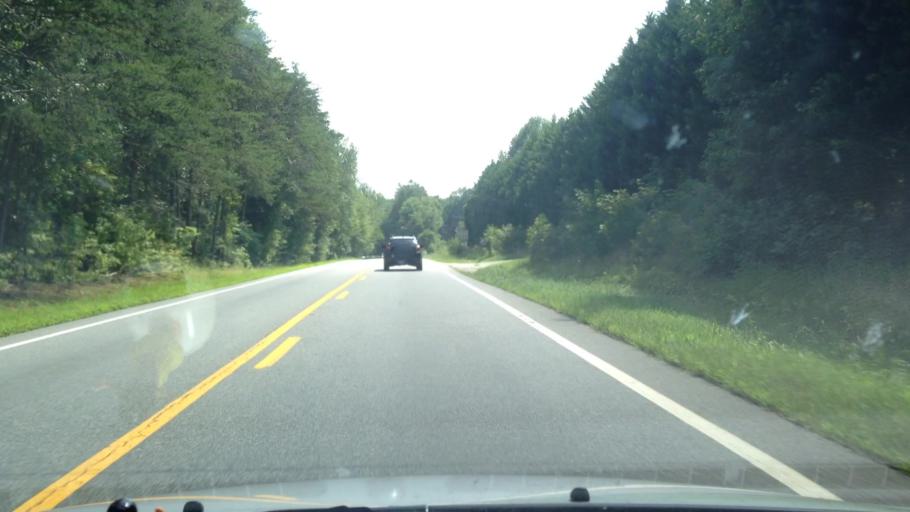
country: US
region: North Carolina
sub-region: Guilford County
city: Oak Ridge
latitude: 36.1823
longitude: -79.9874
